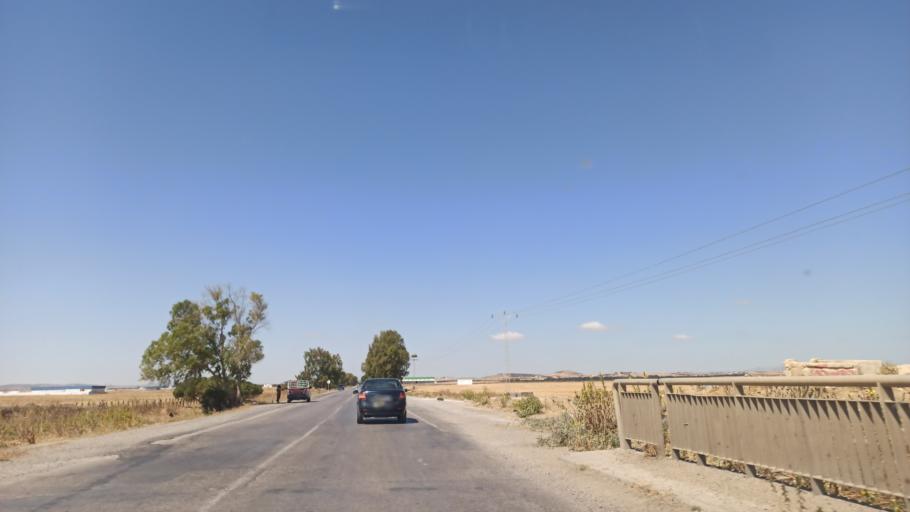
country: TN
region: Tunis
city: Oued Lill
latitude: 36.7433
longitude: 9.9605
